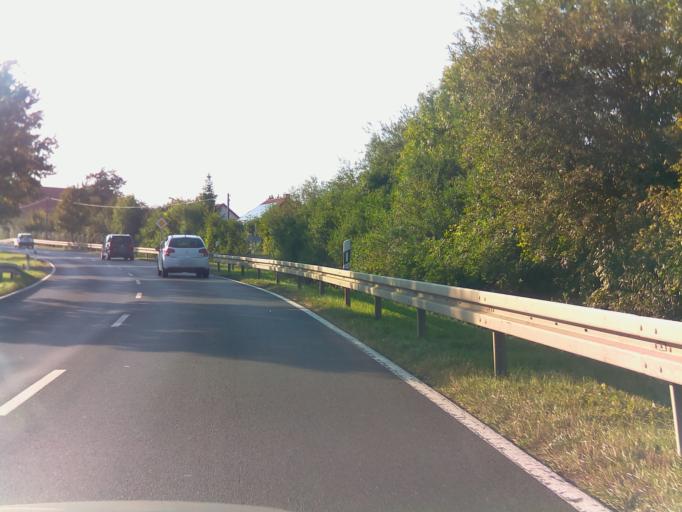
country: DE
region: Bavaria
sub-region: Regierungsbezirk Unterfranken
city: Gaukonigshofen
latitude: 49.6532
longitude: 10.0216
